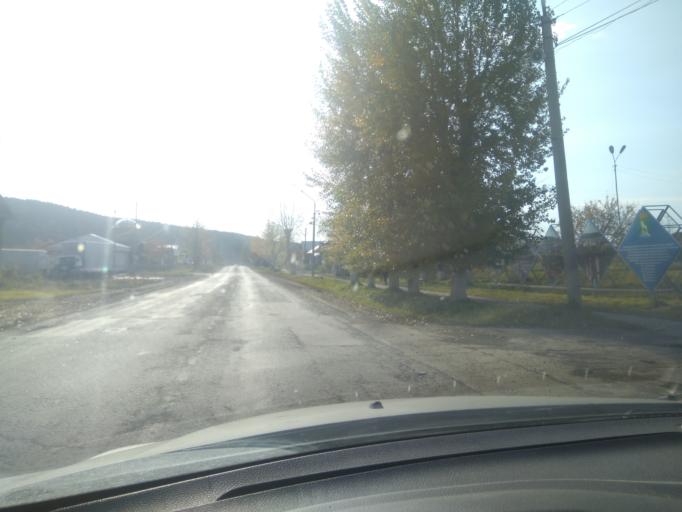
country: RU
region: Sverdlovsk
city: Nizhniye Sergi
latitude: 56.6616
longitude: 59.2996
